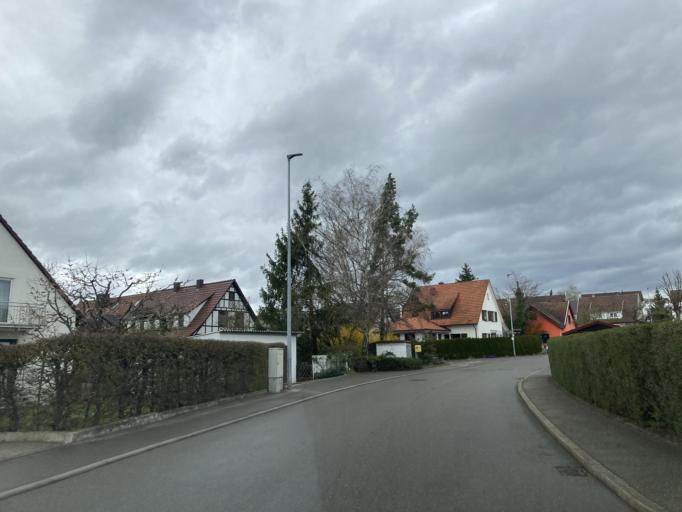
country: DE
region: Baden-Wuerttemberg
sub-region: Tuebingen Region
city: Rottenburg
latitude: 48.5045
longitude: 8.9676
